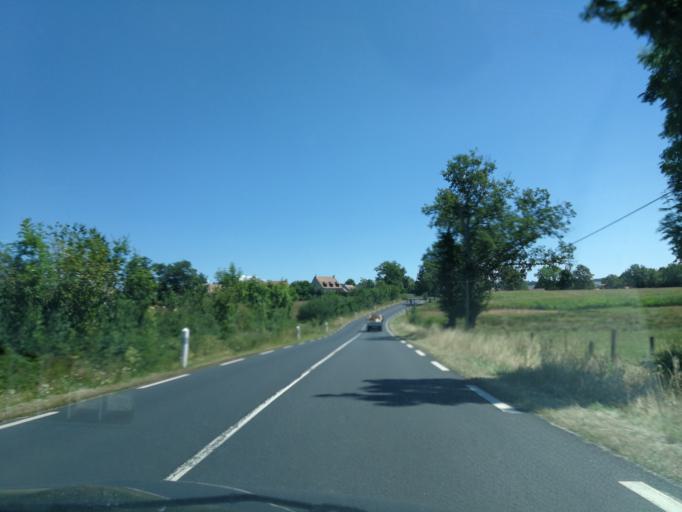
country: FR
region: Auvergne
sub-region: Departement du Cantal
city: Ytrac
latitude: 44.9339
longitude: 2.3733
